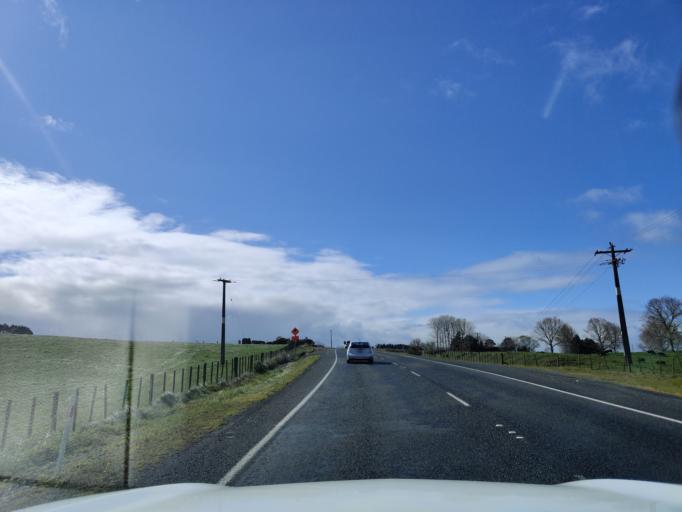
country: NZ
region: Waikato
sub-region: Otorohanga District
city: Otorohanga
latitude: -38.0959
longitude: 175.1856
